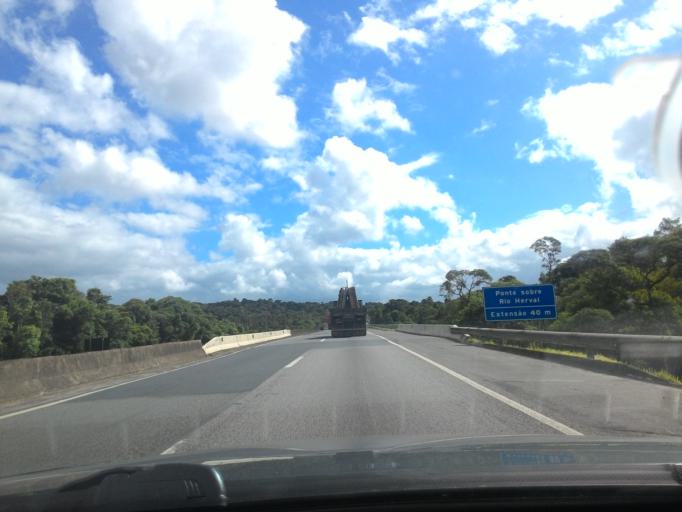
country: BR
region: Sao Paulo
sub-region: Cajati
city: Cajati
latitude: -24.9184
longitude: -48.2579
